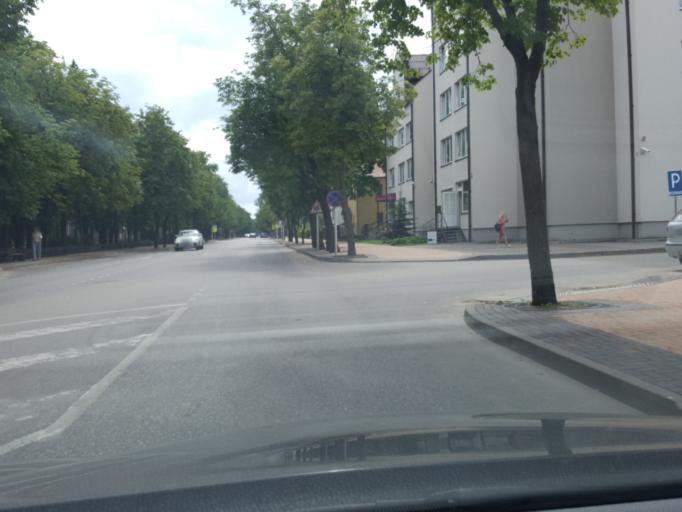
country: LT
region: Alytaus apskritis
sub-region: Alytus
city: Alytus
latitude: 54.3951
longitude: 24.0457
